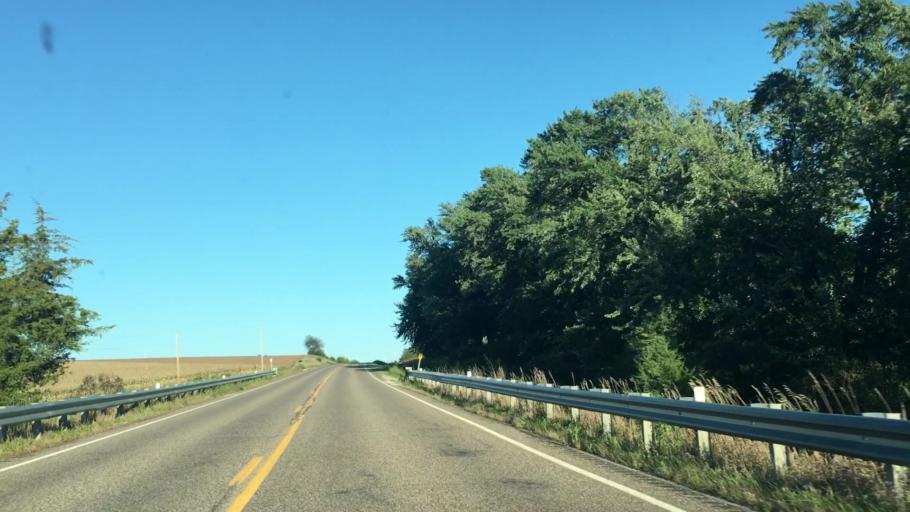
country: US
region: Minnesota
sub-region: Fillmore County
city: Chatfield
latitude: 43.8545
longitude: -92.1246
